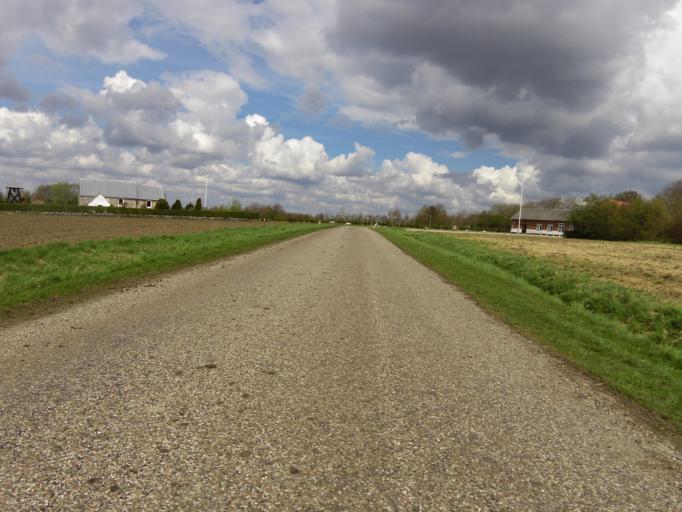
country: DK
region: South Denmark
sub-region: Tonder Kommune
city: Toftlund
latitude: 55.2100
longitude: 9.1353
